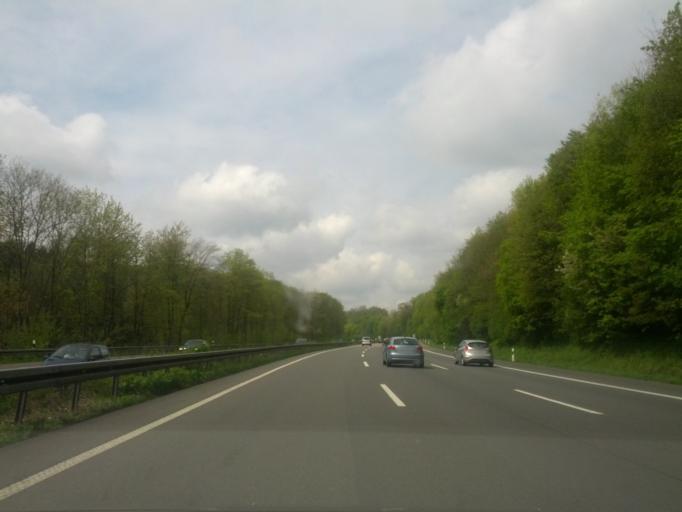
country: DE
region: North Rhine-Westphalia
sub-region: Regierungsbezirk Koln
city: Overath
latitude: 50.9469
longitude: 7.2820
